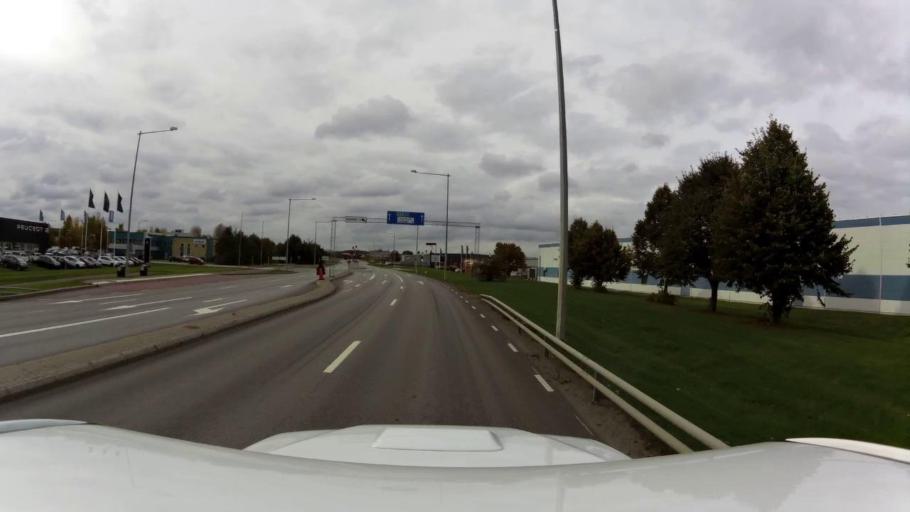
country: SE
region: OEstergoetland
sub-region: Linkopings Kommun
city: Linkoping
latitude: 58.4300
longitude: 15.5986
